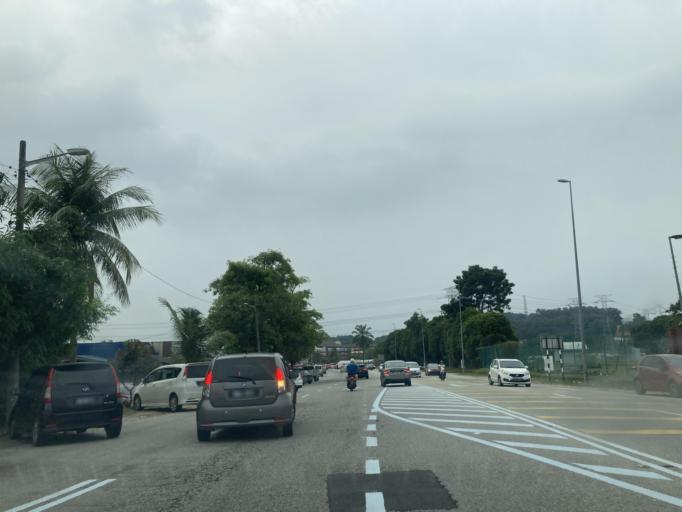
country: MY
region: Selangor
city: Kampung Baru Subang
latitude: 3.2020
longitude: 101.5469
